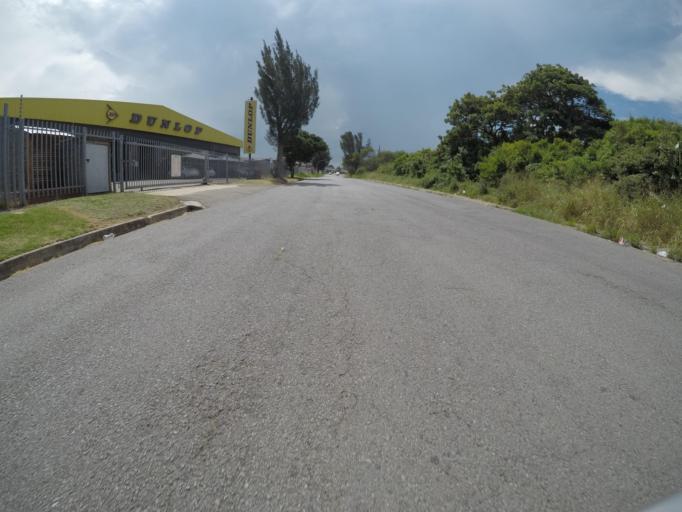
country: ZA
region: Eastern Cape
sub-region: Buffalo City Metropolitan Municipality
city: East London
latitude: -33.0355
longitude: 27.8753
